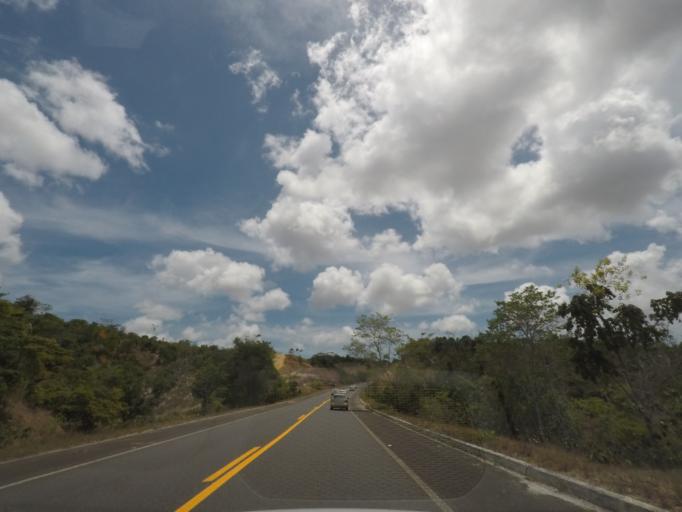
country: BR
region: Sergipe
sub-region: Indiaroba
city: Indiaroba
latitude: -11.5680
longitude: -37.5552
